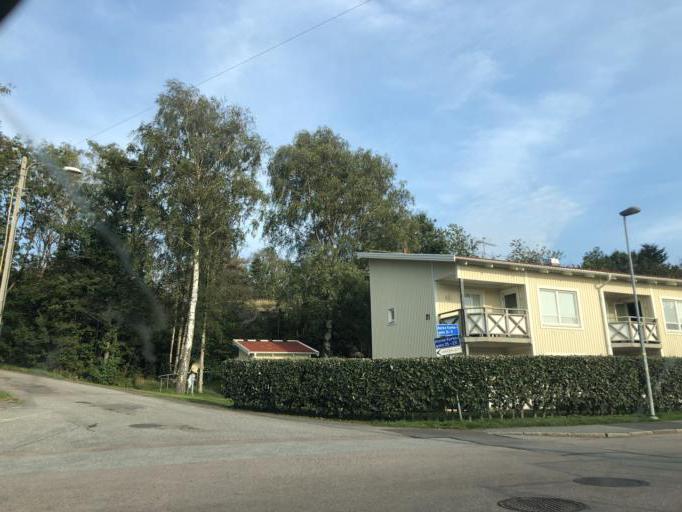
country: SE
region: Vaestra Goetaland
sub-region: Goteborg
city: Goeteborg
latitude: 57.7428
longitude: 11.9787
